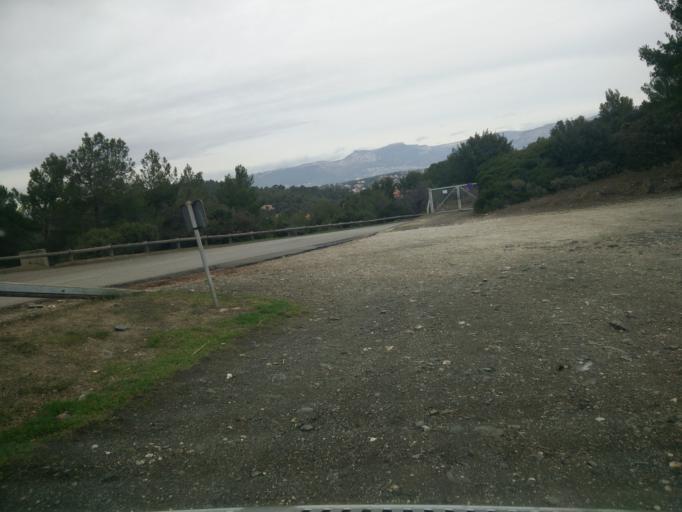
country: FR
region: Provence-Alpes-Cote d'Azur
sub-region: Departement du Var
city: La Seyne-sur-Mer
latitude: 43.0659
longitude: 5.8668
